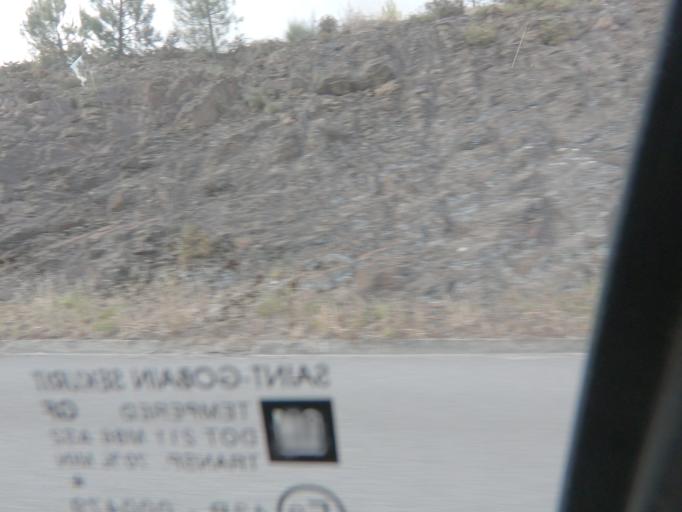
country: PT
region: Porto
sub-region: Paredes
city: Recarei
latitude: 41.1652
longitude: -8.3997
